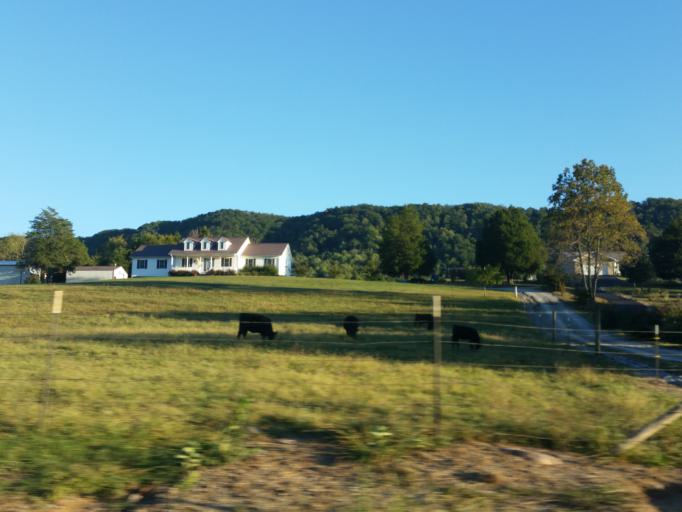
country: US
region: Tennessee
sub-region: Grainger County
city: Rutledge
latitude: 36.3077
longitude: -83.5591
